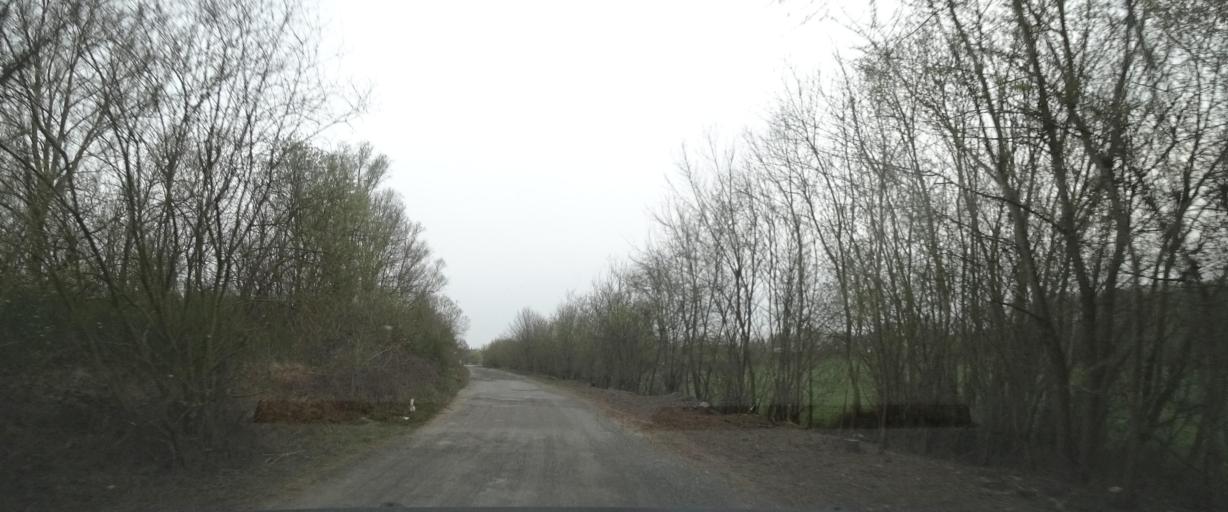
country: BE
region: Wallonia
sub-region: Province du Brabant Wallon
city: Ottignies
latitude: 50.6786
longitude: 4.5525
